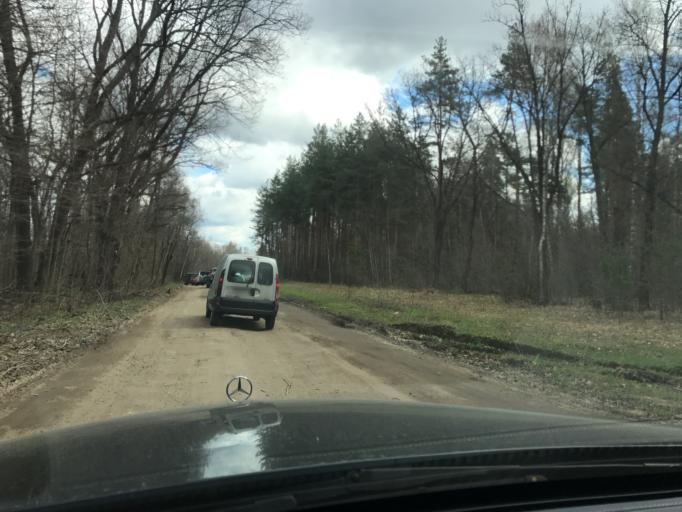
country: RU
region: Vladimir
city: Pokrov
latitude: 55.8769
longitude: 39.2461
